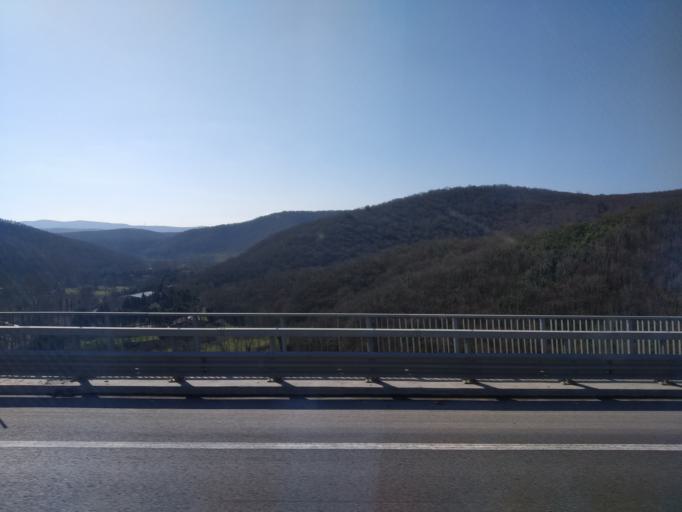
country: TR
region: Istanbul
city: Mahmut Sevket Pasa
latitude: 41.1550
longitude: 29.2664
